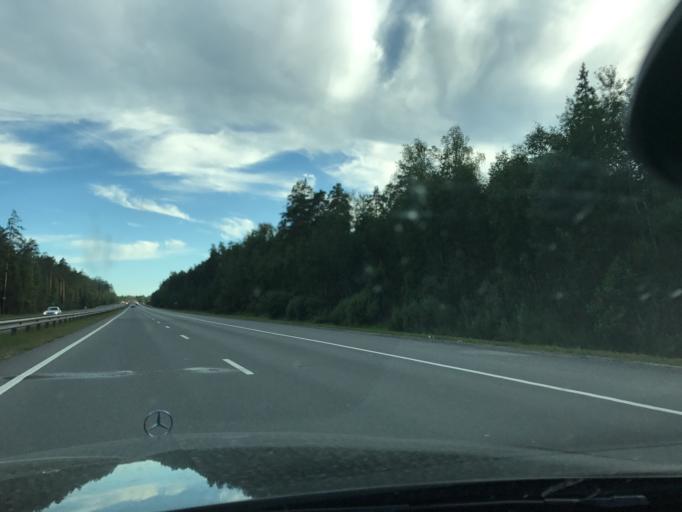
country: RU
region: Vladimir
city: Kommunar
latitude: 56.0722
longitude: 40.4652
